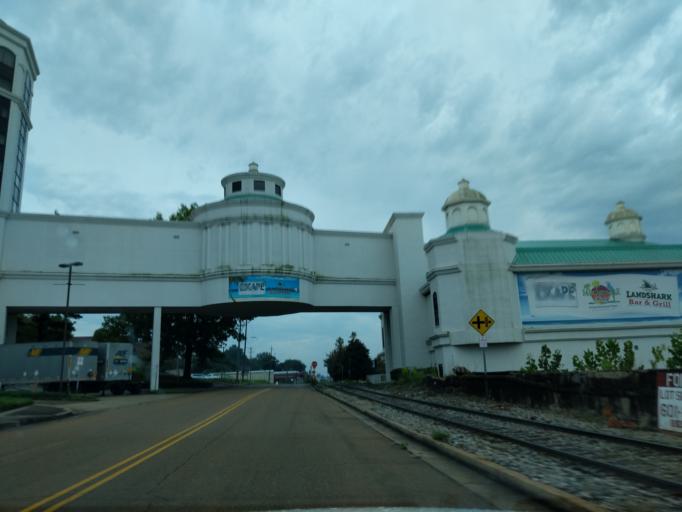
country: US
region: Mississippi
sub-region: Warren County
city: Vicksburg
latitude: 32.3502
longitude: -90.8842
